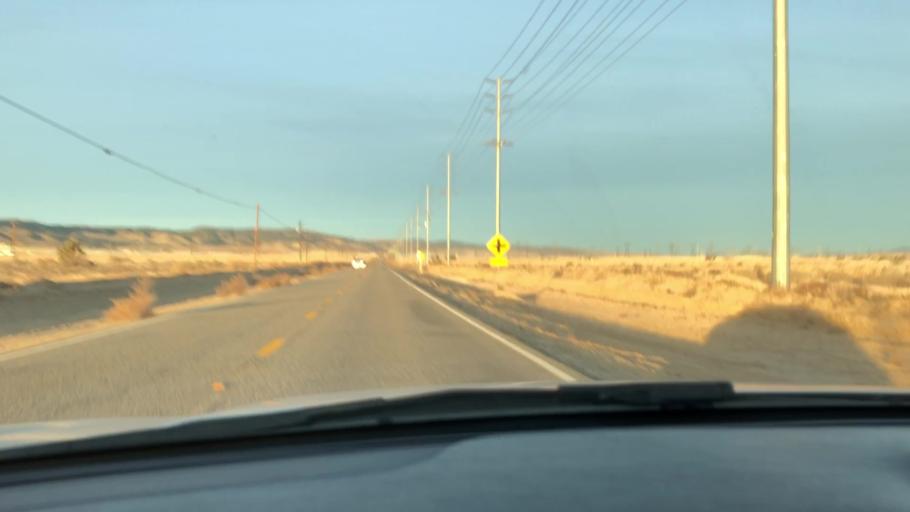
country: US
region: California
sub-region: Los Angeles County
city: Quartz Hill
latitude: 34.6747
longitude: -118.2693
